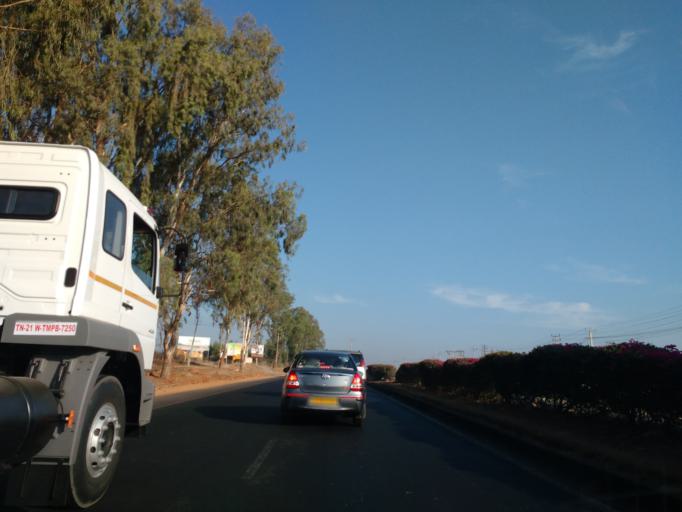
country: IN
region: Karnataka
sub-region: Bangalore Rural
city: Nelamangala
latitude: 13.1579
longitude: 77.3260
